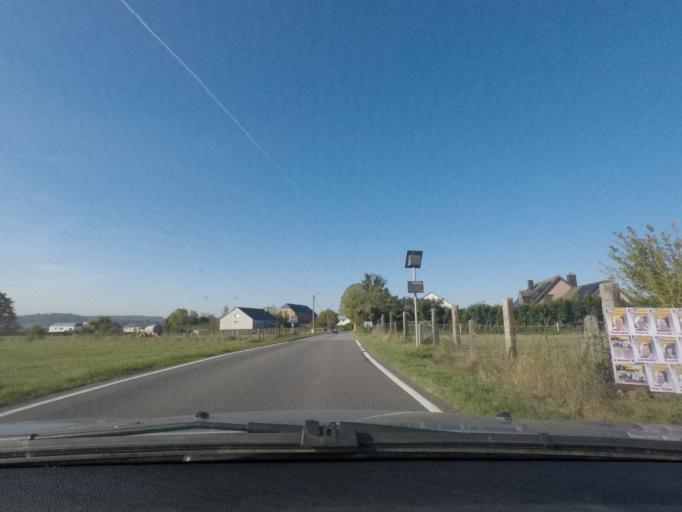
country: BE
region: Wallonia
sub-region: Province du Luxembourg
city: Messancy
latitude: 49.6325
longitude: 5.8075
